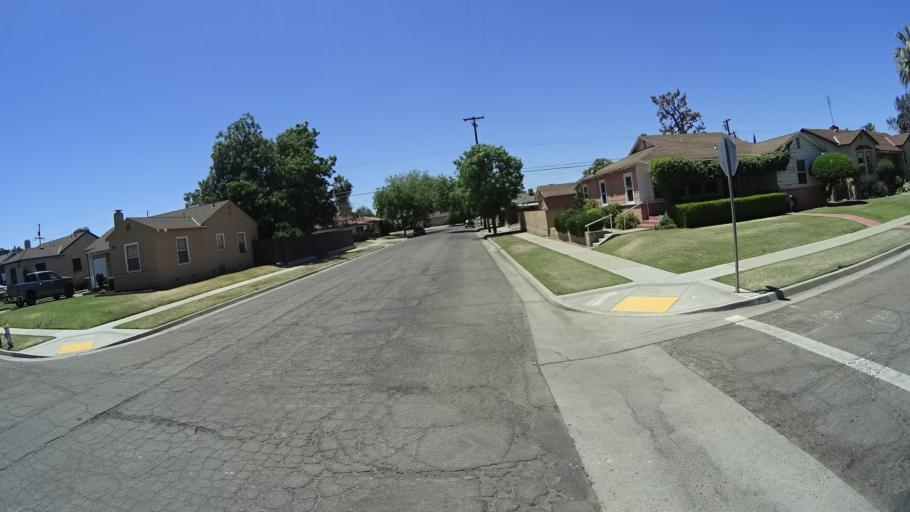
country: US
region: California
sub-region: Fresno County
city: Fresno
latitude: 36.7712
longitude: -119.8199
